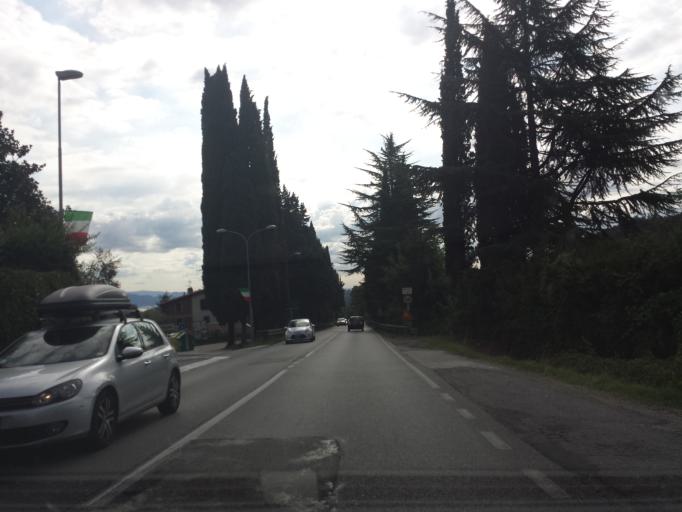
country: IT
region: Lombardy
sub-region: Provincia di Brescia
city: Roe Volciano
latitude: 45.6119
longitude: 10.4908
